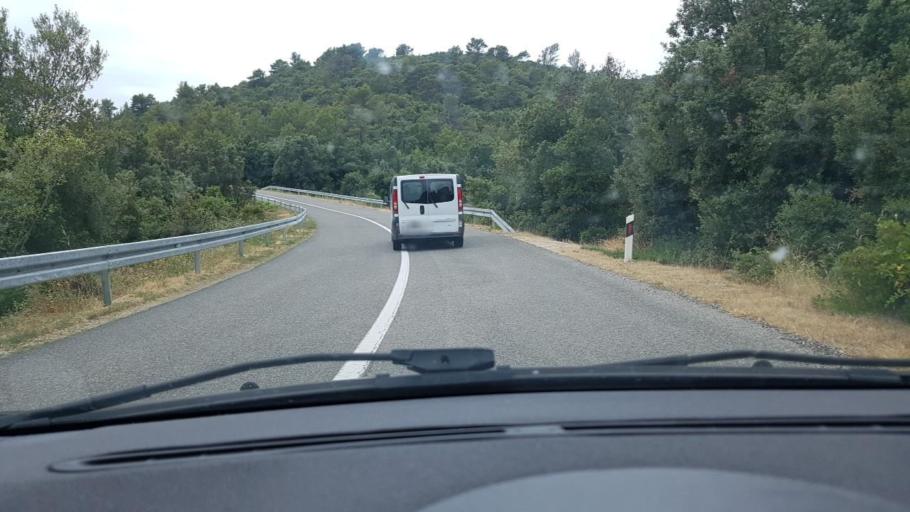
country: HR
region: Dubrovacko-Neretvanska
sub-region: Grad Korcula
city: Zrnovo
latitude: 42.9439
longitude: 17.0252
